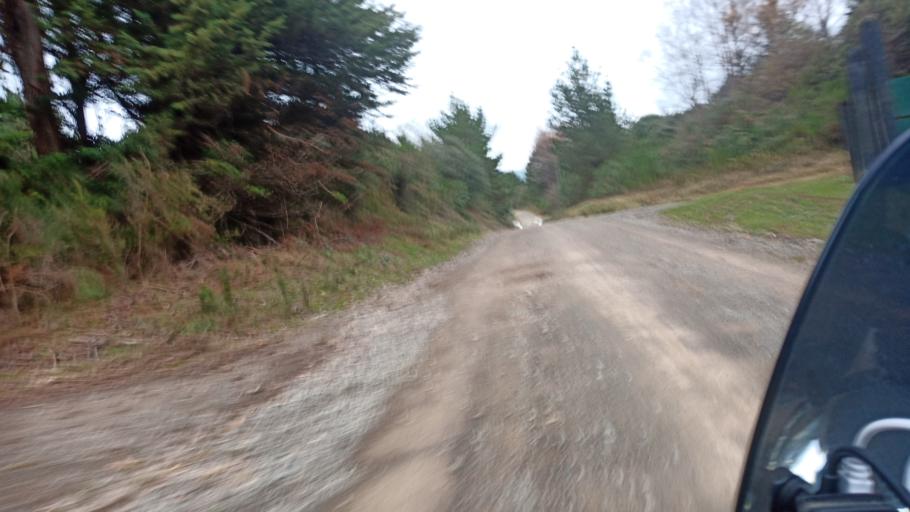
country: NZ
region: Bay of Plenty
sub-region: Whakatane District
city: Murupara
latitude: -38.6356
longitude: 176.7204
